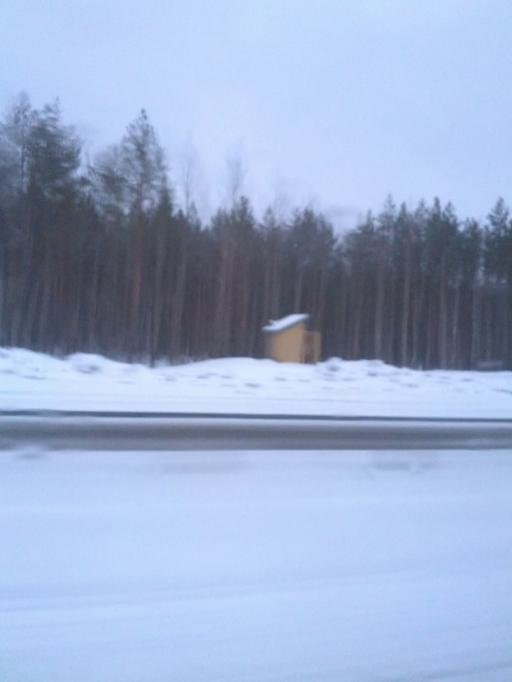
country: RU
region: Mariy-El
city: Surok
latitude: 56.4596
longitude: 48.0906
